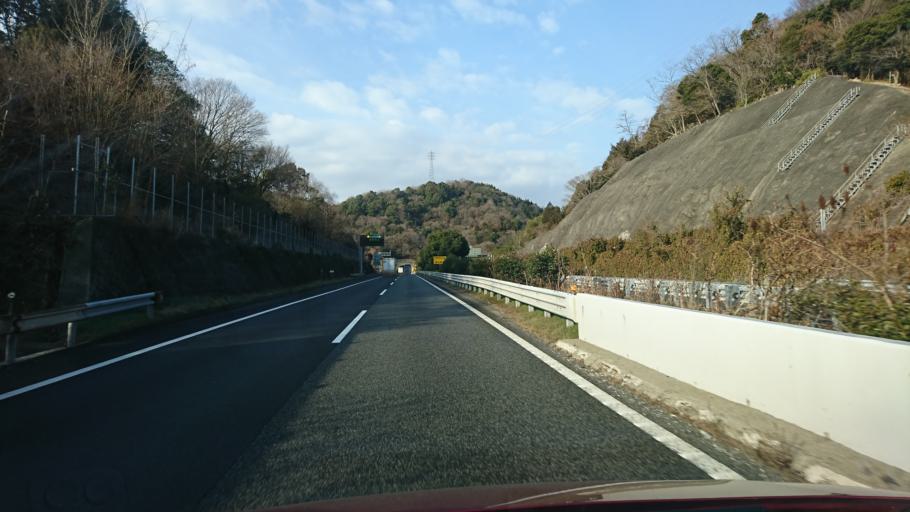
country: JP
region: Hyogo
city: Aioi
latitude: 34.8289
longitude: 134.4849
